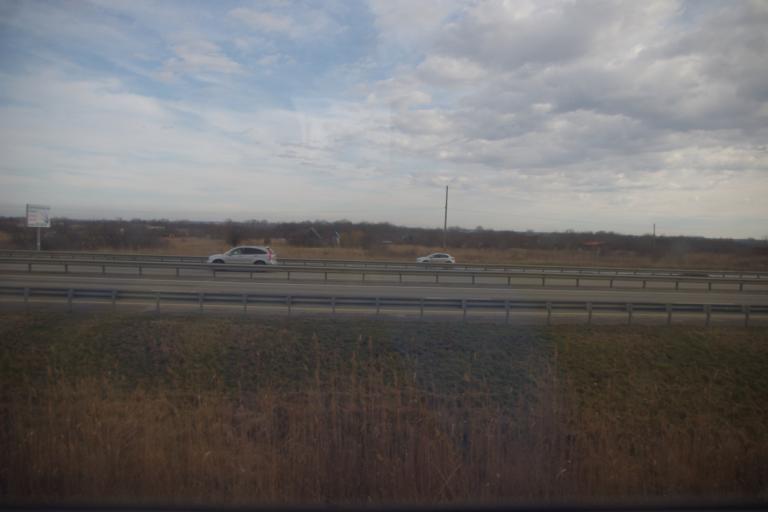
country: RU
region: Adygeya
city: Adygeysk
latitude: 44.8118
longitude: 39.2277
